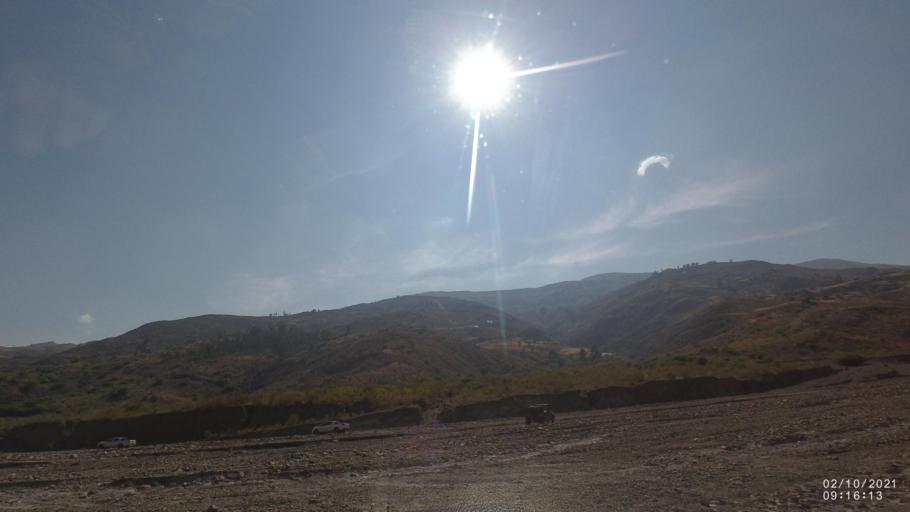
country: BO
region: Cochabamba
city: Irpa Irpa
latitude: -17.8825
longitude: -66.3050
